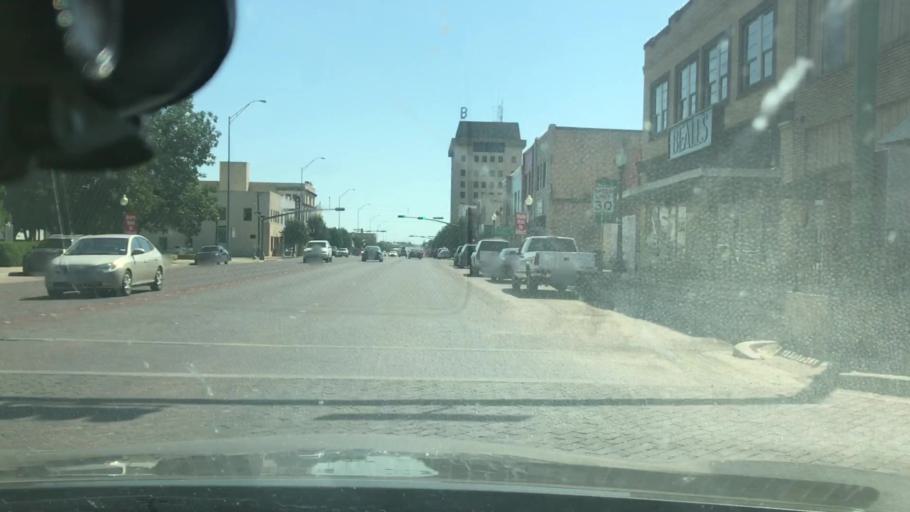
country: US
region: Texas
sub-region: Stephens County
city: Breckenridge
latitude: 32.7554
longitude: -98.9050
